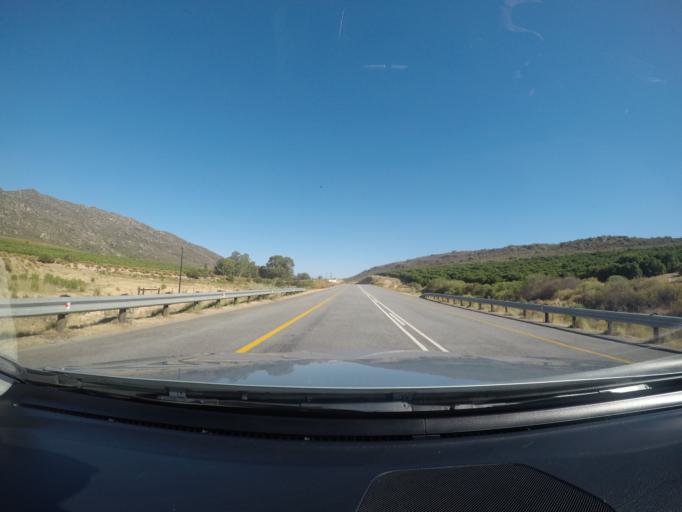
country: ZA
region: Western Cape
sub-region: West Coast District Municipality
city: Clanwilliam
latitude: -32.3585
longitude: 18.9367
